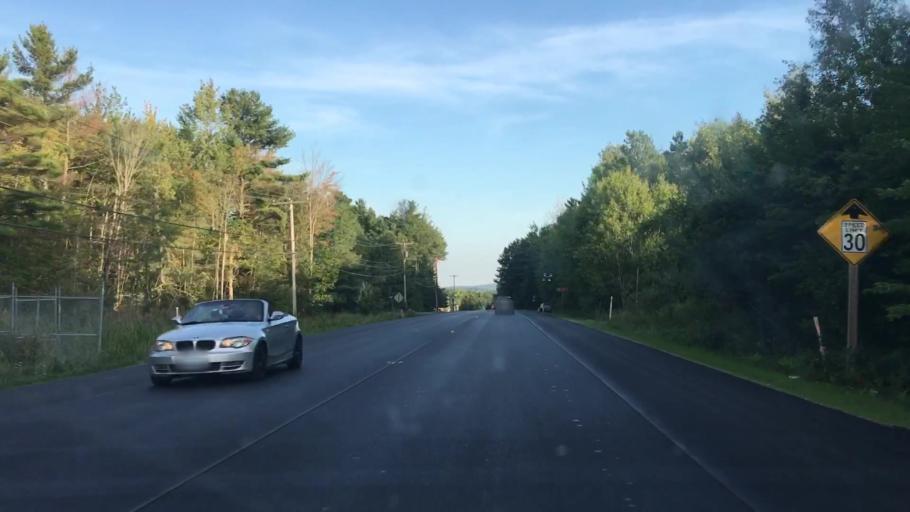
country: US
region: Maine
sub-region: Penobscot County
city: Hampden
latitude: 44.7569
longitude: -68.8432
